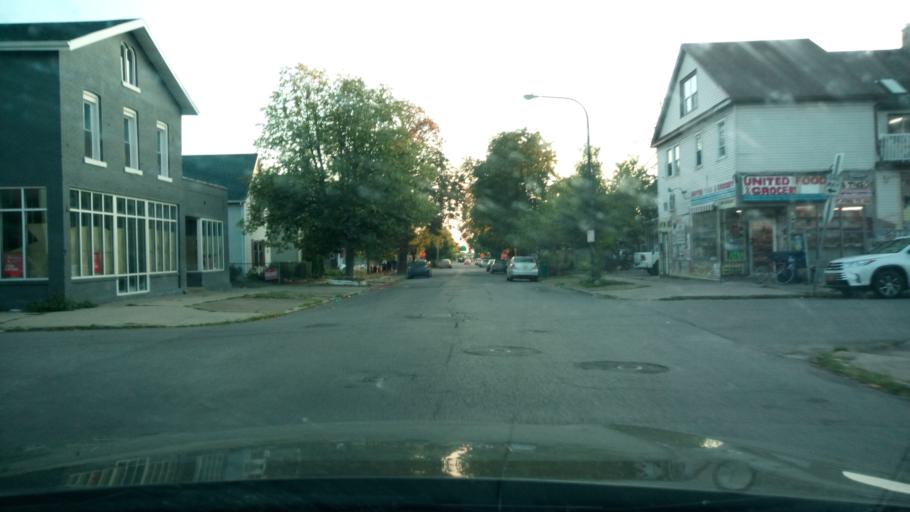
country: US
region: New York
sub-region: Erie County
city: Buffalo
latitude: 42.8945
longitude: -78.8827
